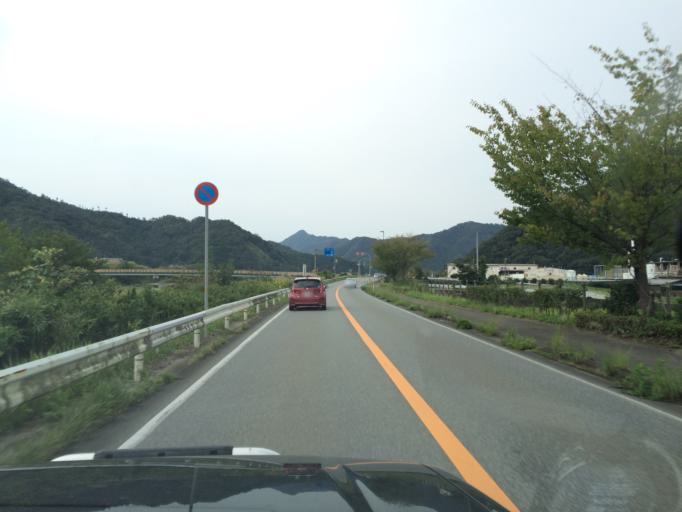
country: JP
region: Hyogo
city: Toyooka
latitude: 35.3911
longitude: 134.7972
